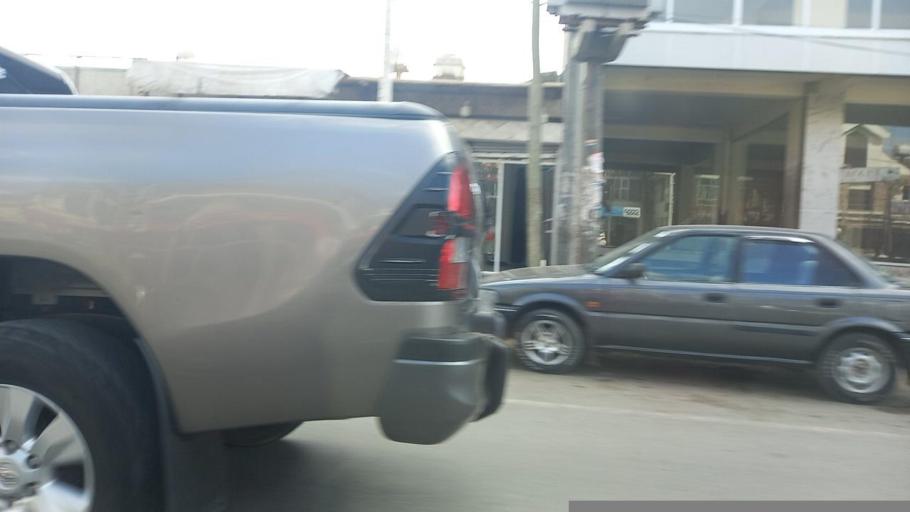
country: ET
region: Adis Abeba
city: Addis Ababa
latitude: 9.0109
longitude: 38.8382
